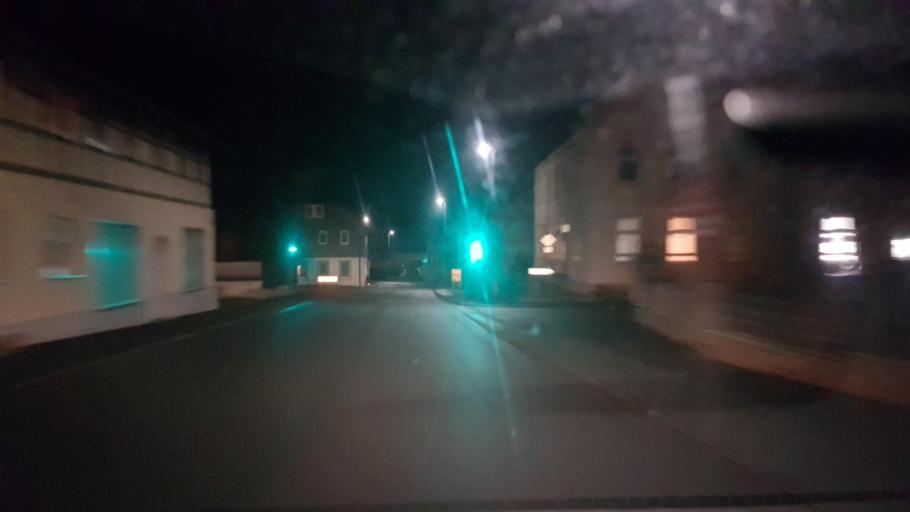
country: DE
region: Bavaria
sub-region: Regierungsbezirk Unterfranken
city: Maroldsweisach
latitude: 50.1984
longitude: 10.6579
